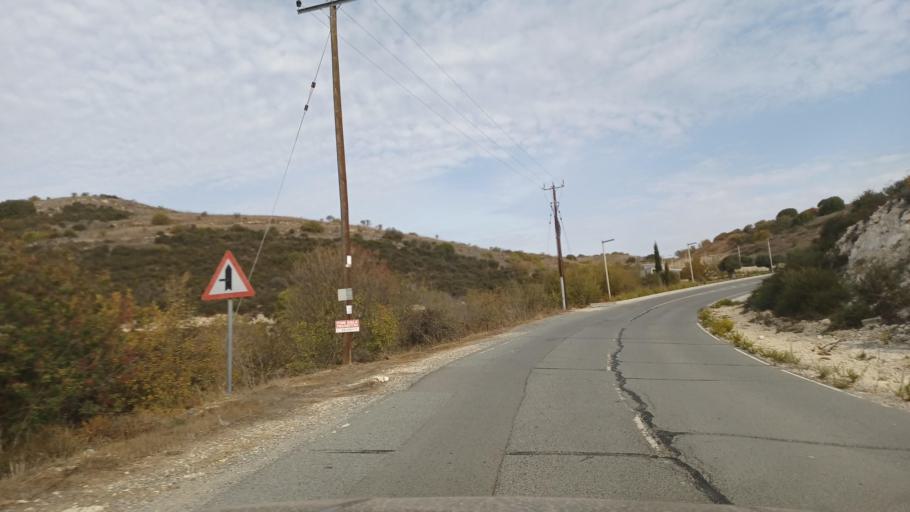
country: CY
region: Pafos
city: Mesogi
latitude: 34.8013
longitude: 32.5082
